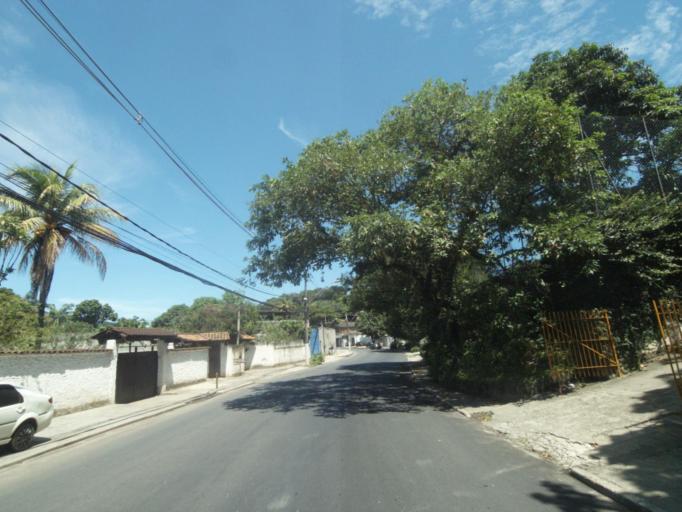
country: BR
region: Rio de Janeiro
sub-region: Sao Goncalo
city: Sao Goncalo
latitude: -22.9034
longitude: -42.9856
